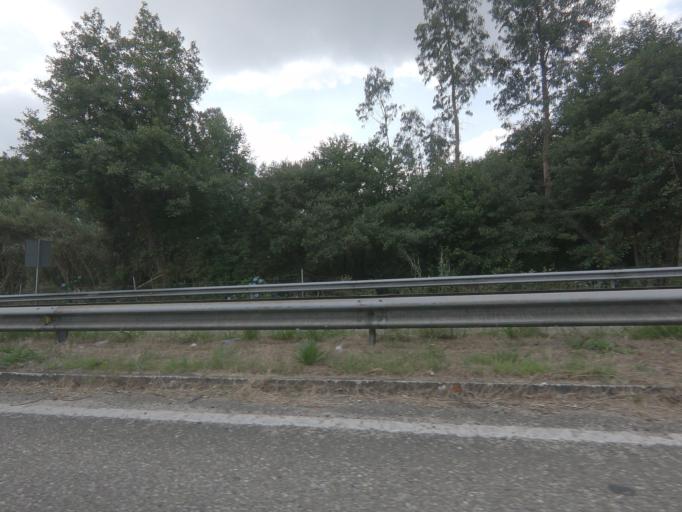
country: PT
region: Viana do Castelo
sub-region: Valenca
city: Valenca
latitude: 42.0391
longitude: -8.6576
